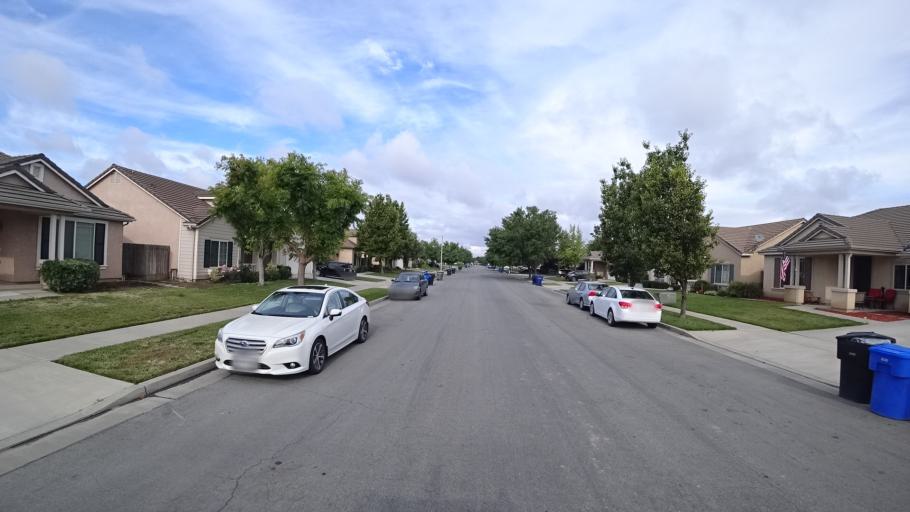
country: US
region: California
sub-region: Kings County
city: Hanford
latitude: 36.3349
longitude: -119.6759
